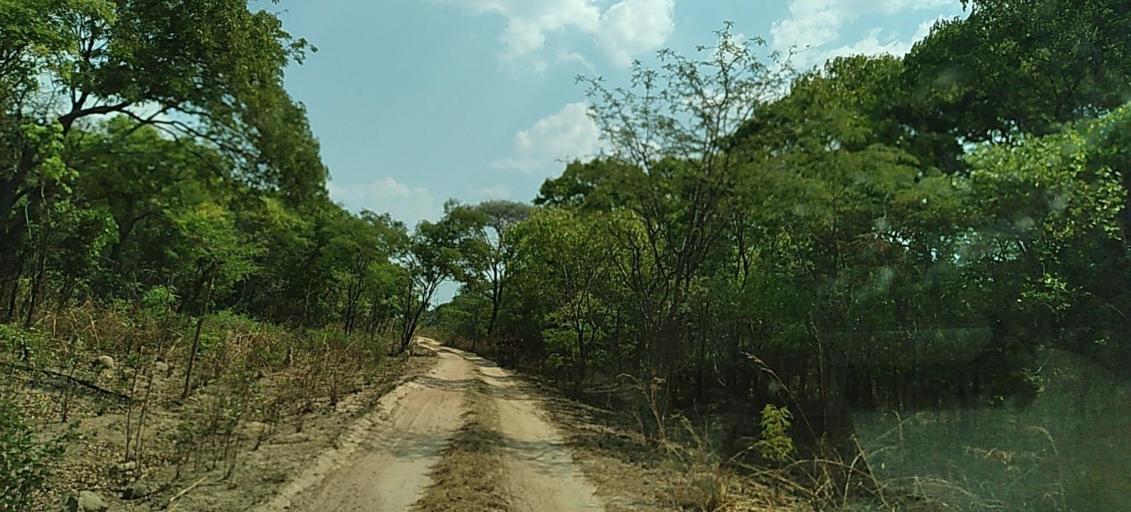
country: ZM
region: Copperbelt
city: Mpongwe
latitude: -13.8689
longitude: 27.9245
